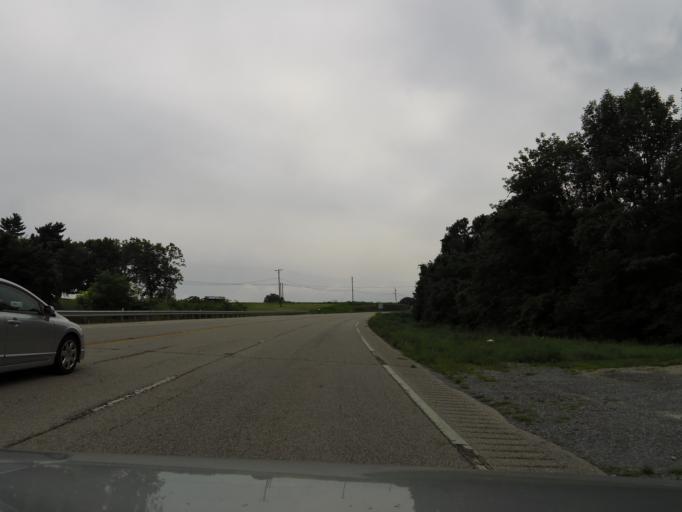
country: US
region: Kentucky
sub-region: Mason County
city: Maysville
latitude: 38.5640
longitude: -83.8222
